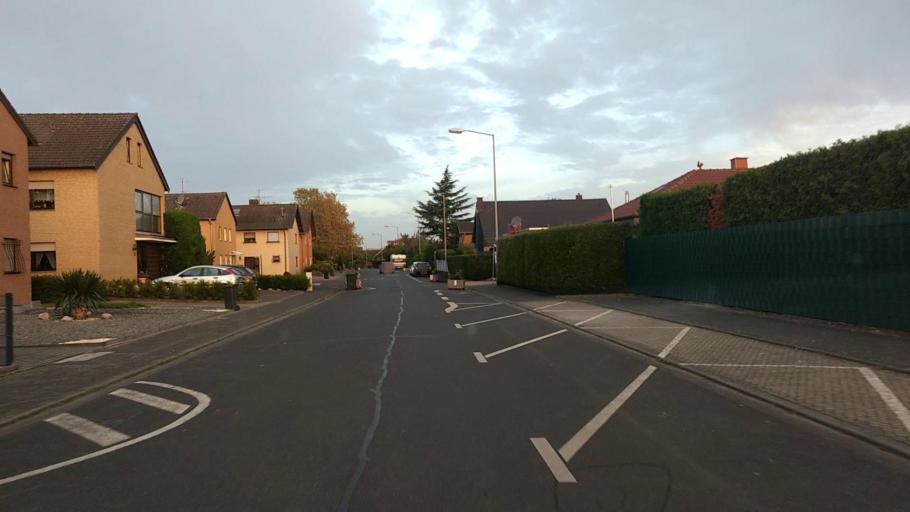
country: DE
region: North Rhine-Westphalia
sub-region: Regierungsbezirk Koln
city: Bergheim
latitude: 50.9321
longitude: 6.6777
